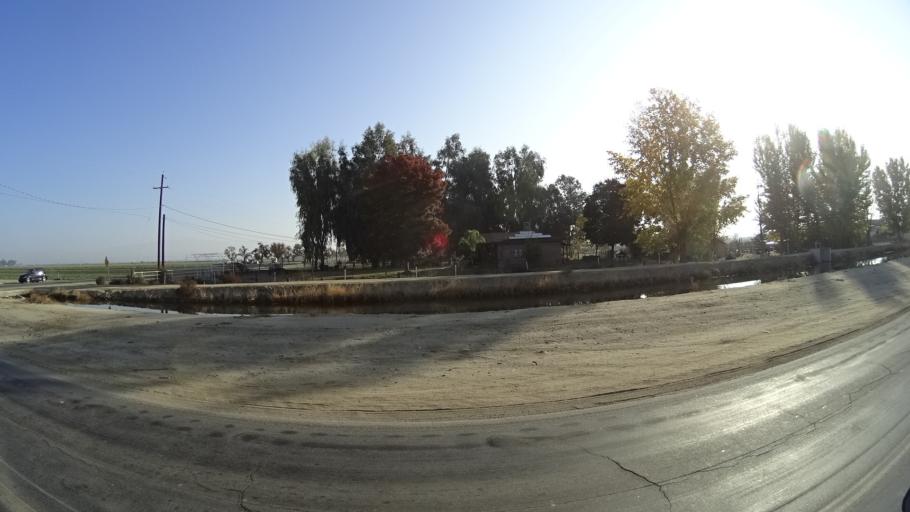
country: US
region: California
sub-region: Kern County
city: Greenfield
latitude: 35.2520
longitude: -118.9855
